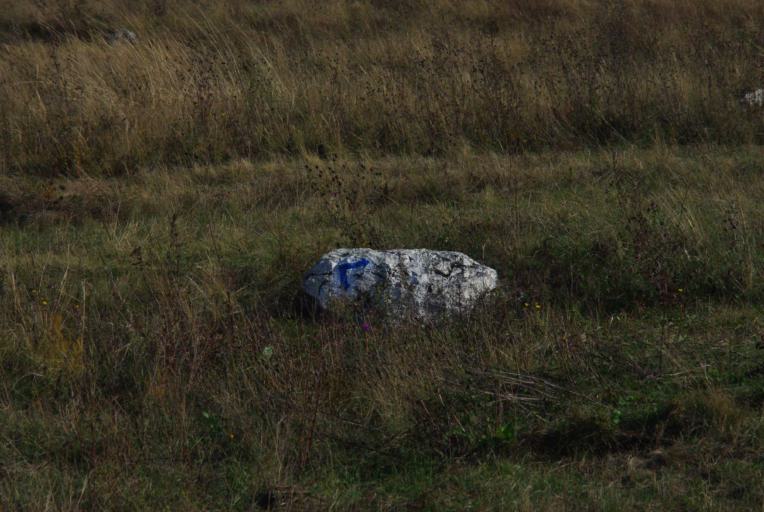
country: HU
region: Komarom-Esztergom
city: Kesztolc
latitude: 47.7237
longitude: 18.7974
